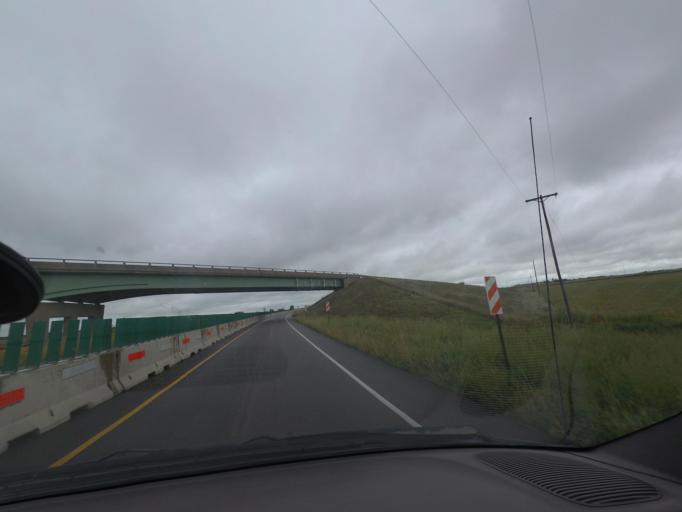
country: US
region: Illinois
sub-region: Piatt County
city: Cerro Gordo
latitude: 40.0112
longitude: -88.7719
